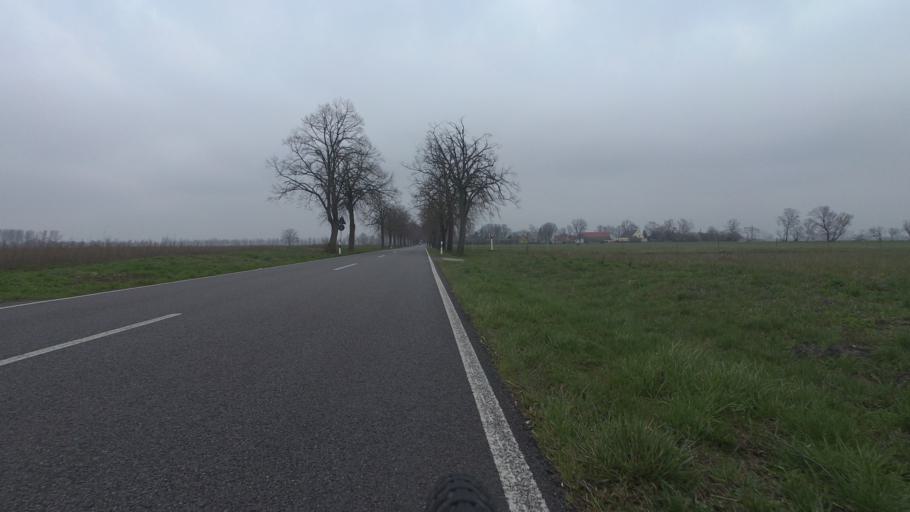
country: DE
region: Brandenburg
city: Nauen
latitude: 52.6336
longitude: 12.8506
